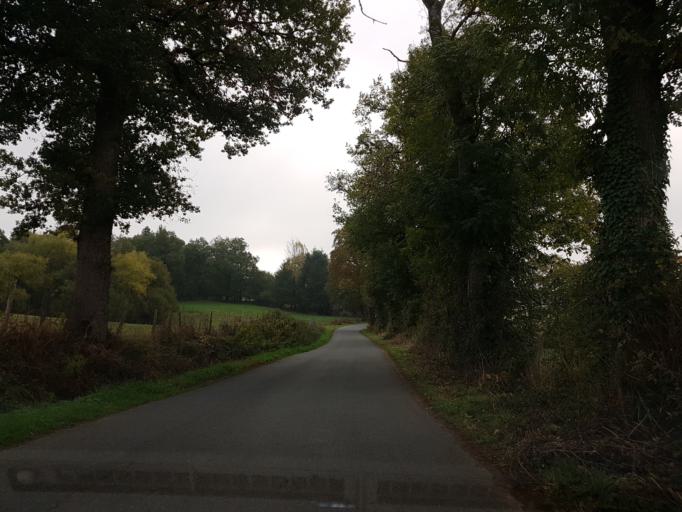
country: FR
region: Poitou-Charentes
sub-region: Departement de la Charente
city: Chabanais
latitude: 45.8861
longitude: 0.7199
